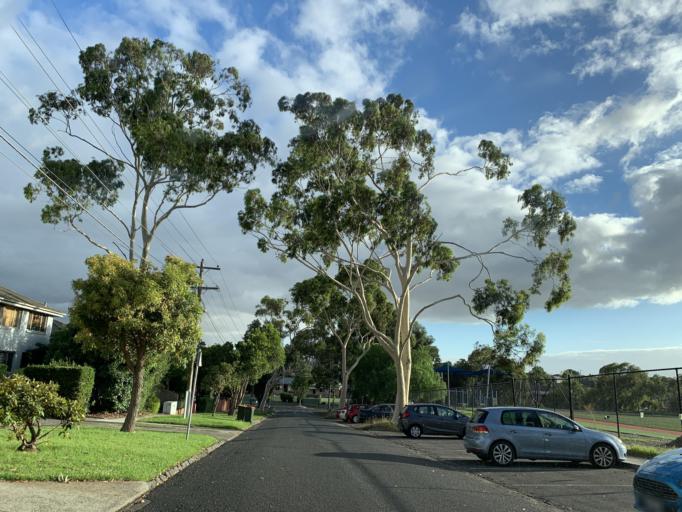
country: AU
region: Victoria
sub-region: Moonee Valley
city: Essendon North
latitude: -37.7402
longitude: 144.9029
